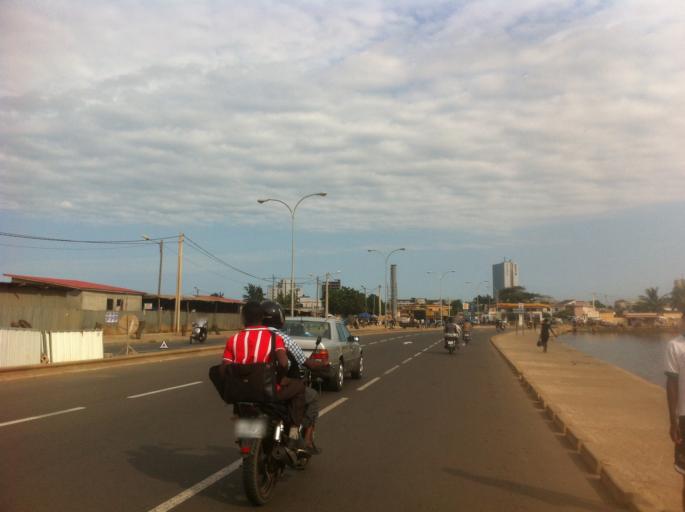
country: TG
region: Maritime
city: Lome
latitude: 6.1386
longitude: 1.2103
